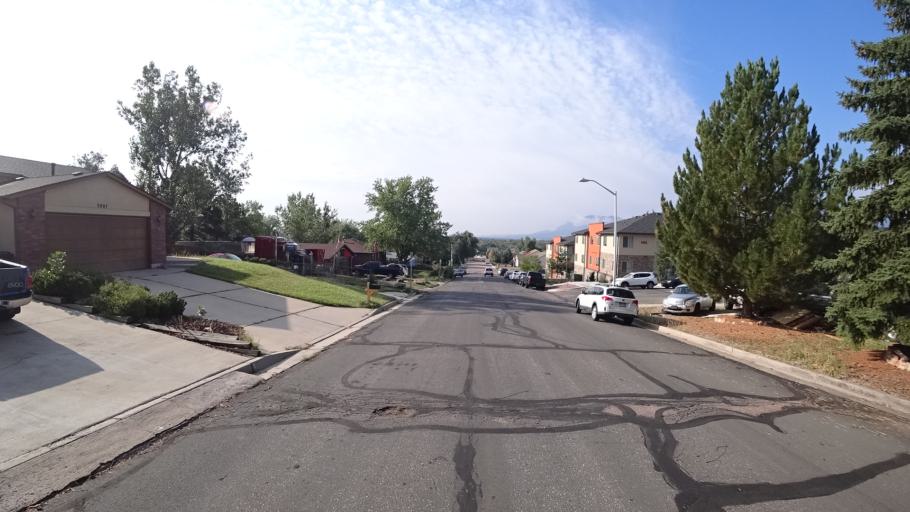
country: US
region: Colorado
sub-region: El Paso County
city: Colorado Springs
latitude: 38.8868
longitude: -104.8034
